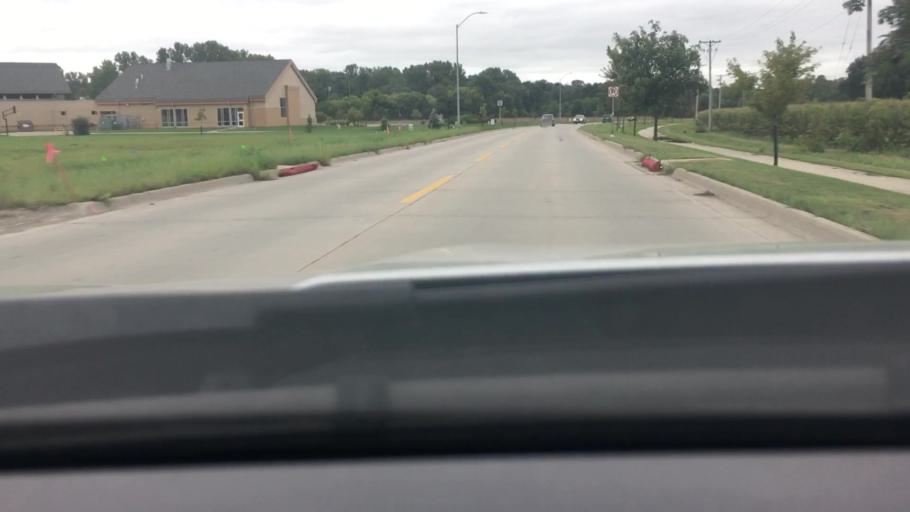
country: US
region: Iowa
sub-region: Pottawattamie County
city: Council Bluffs
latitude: 41.2656
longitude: -95.8039
